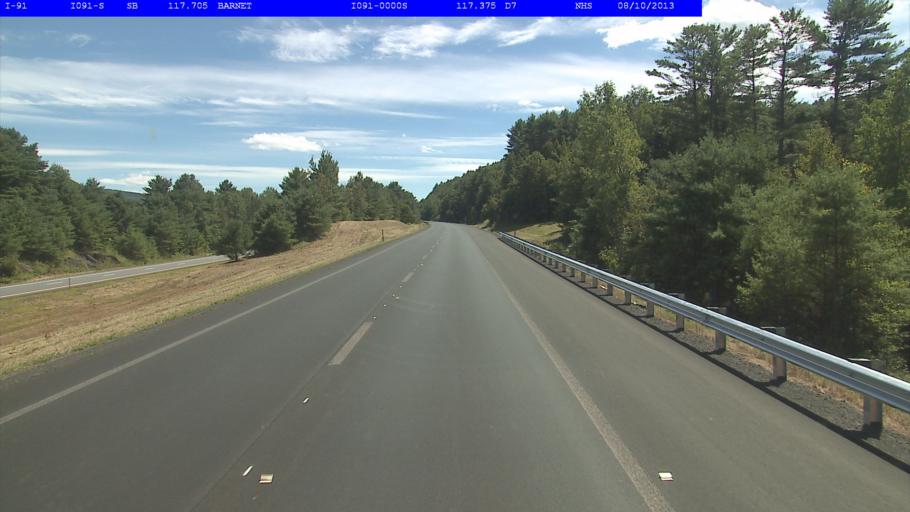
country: US
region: New Hampshire
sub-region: Grafton County
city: Woodsville
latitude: 44.2620
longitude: -72.0678
